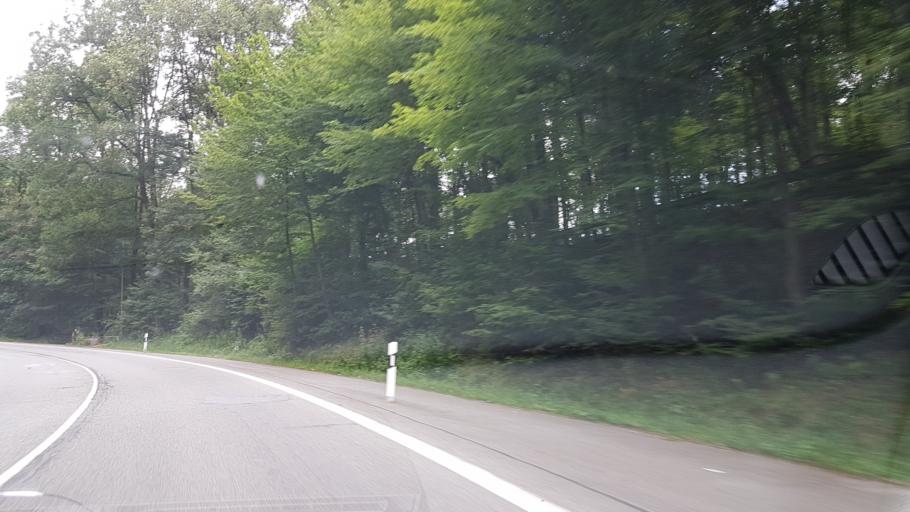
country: DE
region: Saarland
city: Sulzbach
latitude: 49.3067
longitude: 7.0522
